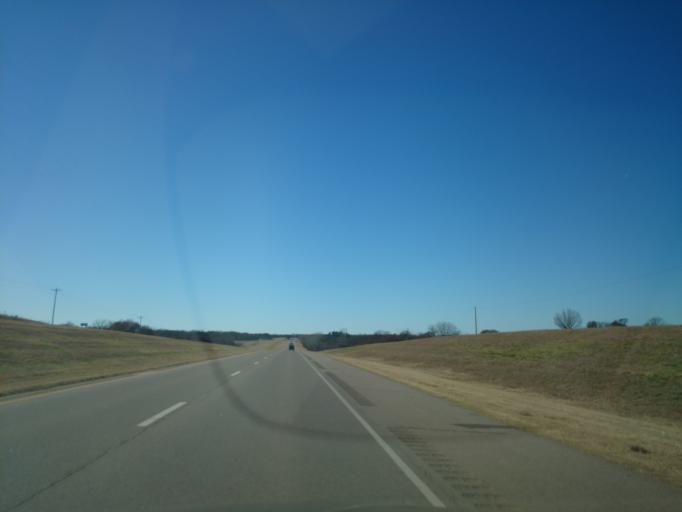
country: US
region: Oklahoma
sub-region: Payne County
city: Stillwater
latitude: 36.1119
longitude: -97.1953
